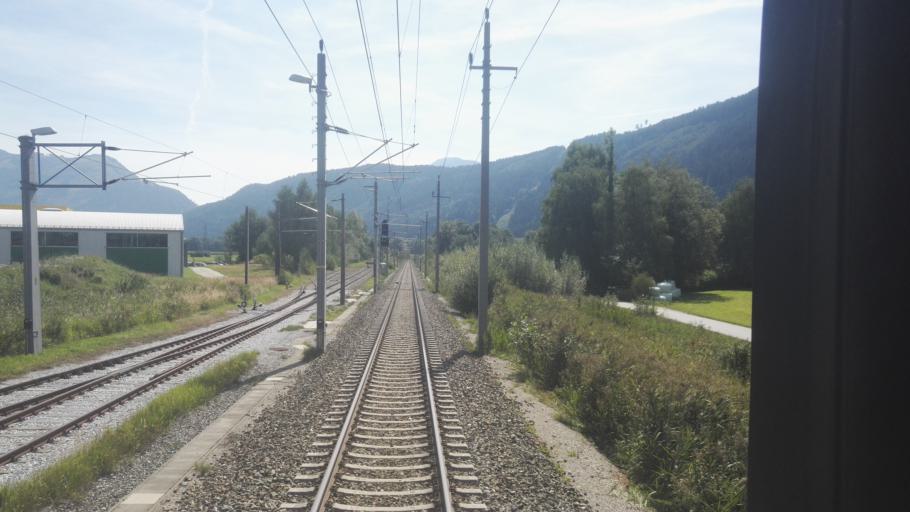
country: AT
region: Styria
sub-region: Politischer Bezirk Liezen
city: Liezen
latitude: 47.5581
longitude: 14.2506
